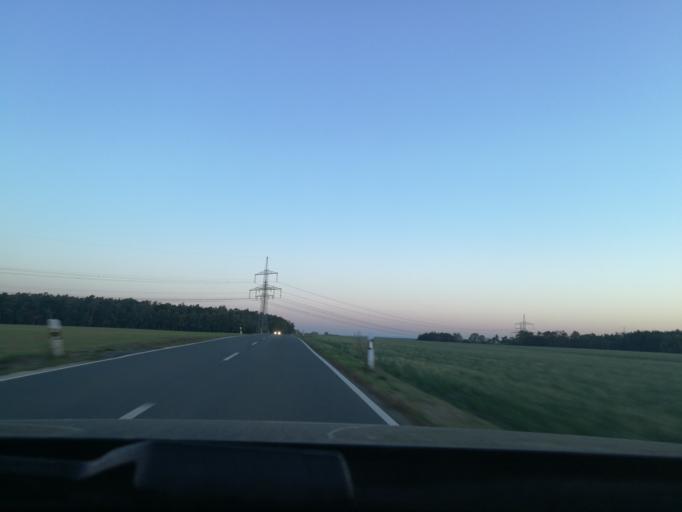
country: DE
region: Bavaria
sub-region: Regierungsbezirk Mittelfranken
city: Obermichelbach
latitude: 49.5406
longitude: 10.9113
